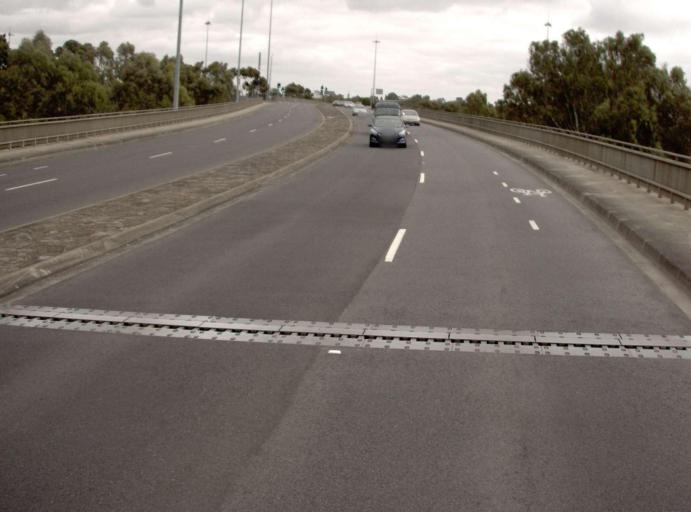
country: AU
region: Victoria
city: Ivanhoe East
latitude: -37.7866
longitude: 145.0648
